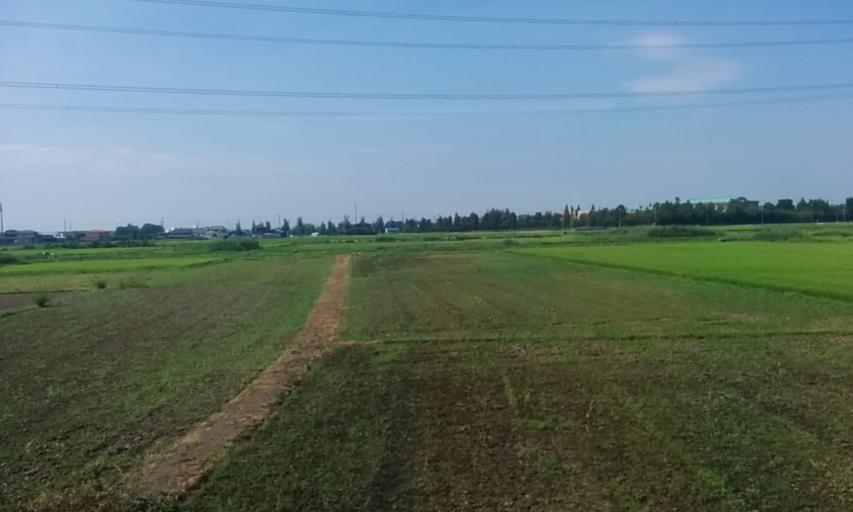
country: JP
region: Saitama
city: Kukichuo
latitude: 36.1052
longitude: 139.6475
